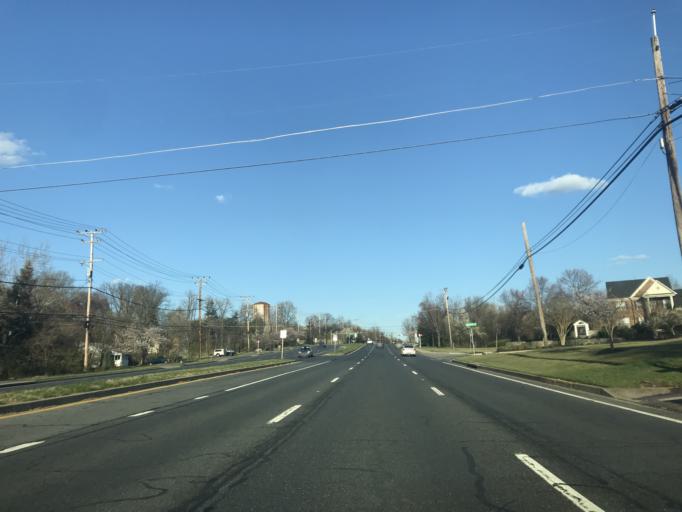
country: US
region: Maryland
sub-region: Prince George's County
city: Springdale
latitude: 38.9565
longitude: -76.8169
